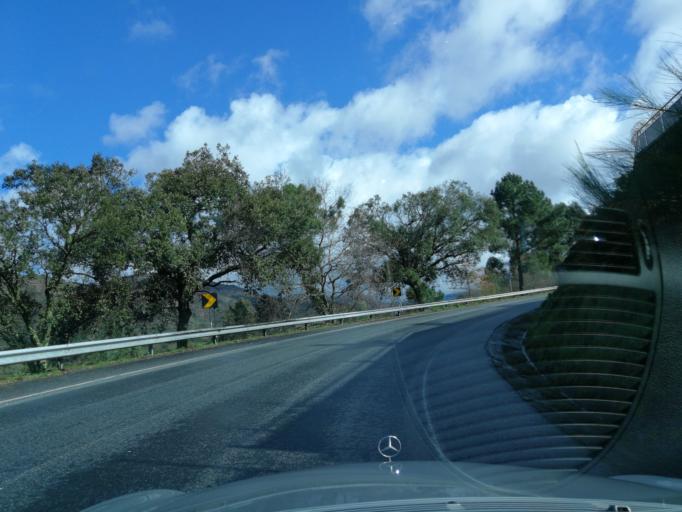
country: PT
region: Braga
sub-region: Terras de Bouro
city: Antas
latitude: 41.8343
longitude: -8.2999
